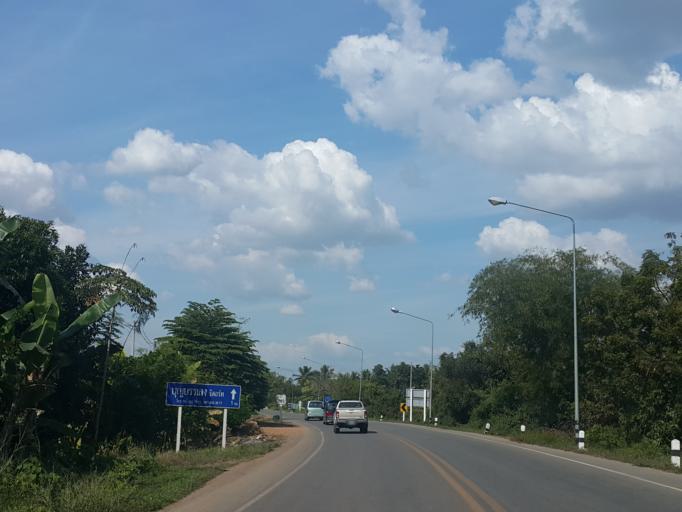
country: TH
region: Sukhothai
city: Sawankhalok
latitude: 17.2839
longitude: 99.8348
